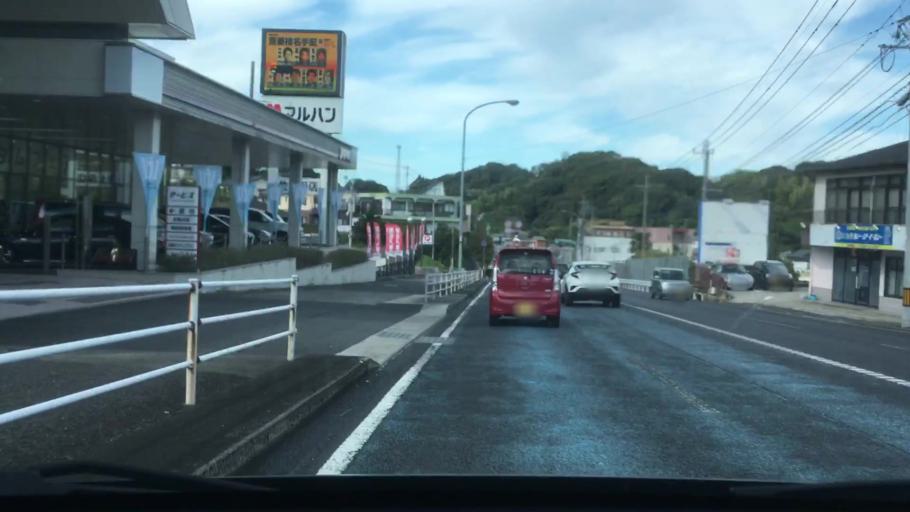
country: JP
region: Nagasaki
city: Sasebo
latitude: 33.1585
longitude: 129.7631
